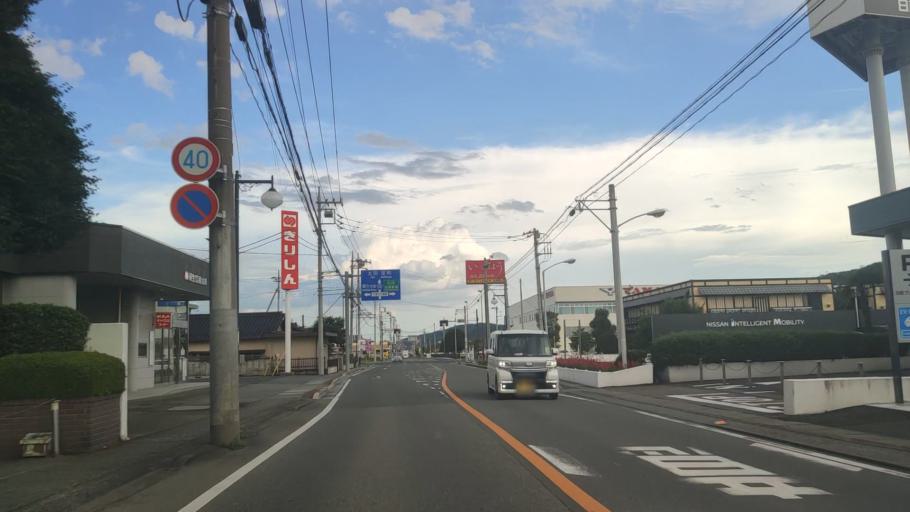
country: JP
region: Gunma
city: Kiryu
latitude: 36.3941
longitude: 139.3268
